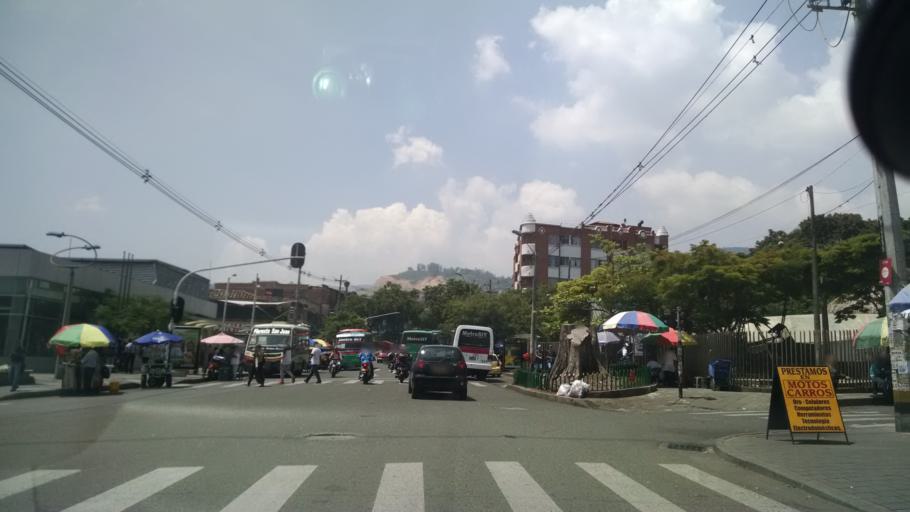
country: CO
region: Antioquia
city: Medellin
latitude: 6.2577
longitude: -75.6144
